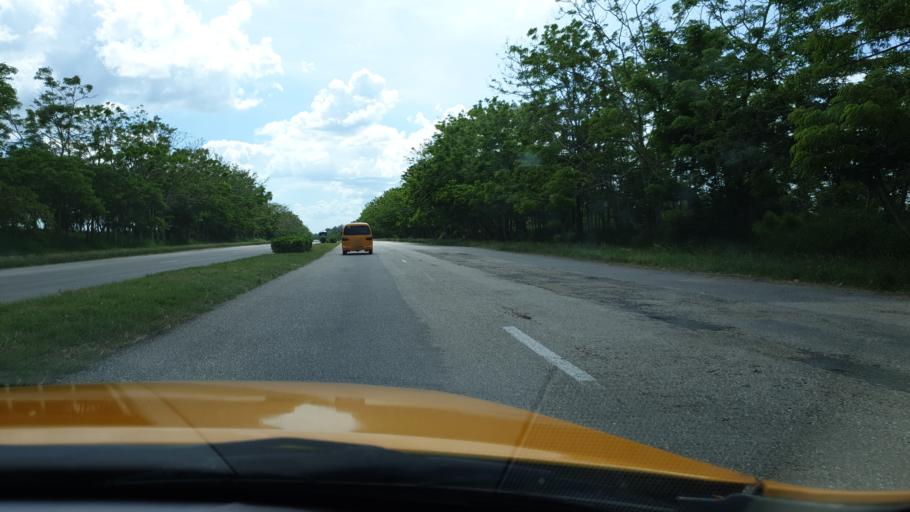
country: CU
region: Cienfuegos
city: Cruces
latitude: 22.4554
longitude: -80.3093
